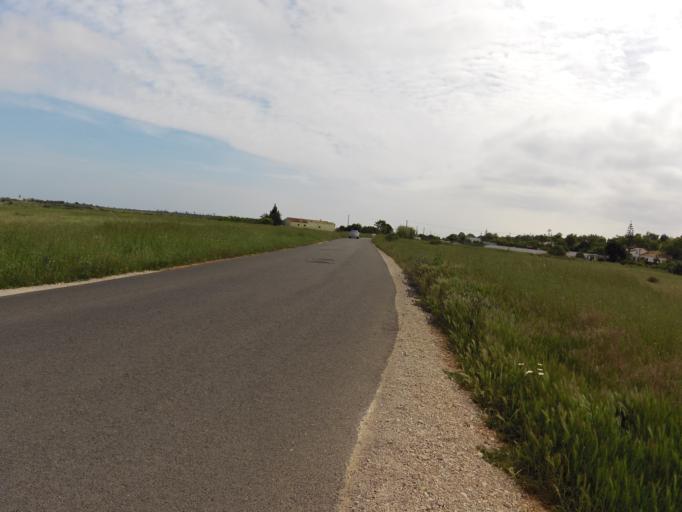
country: PT
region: Faro
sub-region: Silves
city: Armacao de Pera
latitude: 37.1148
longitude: -8.3469
